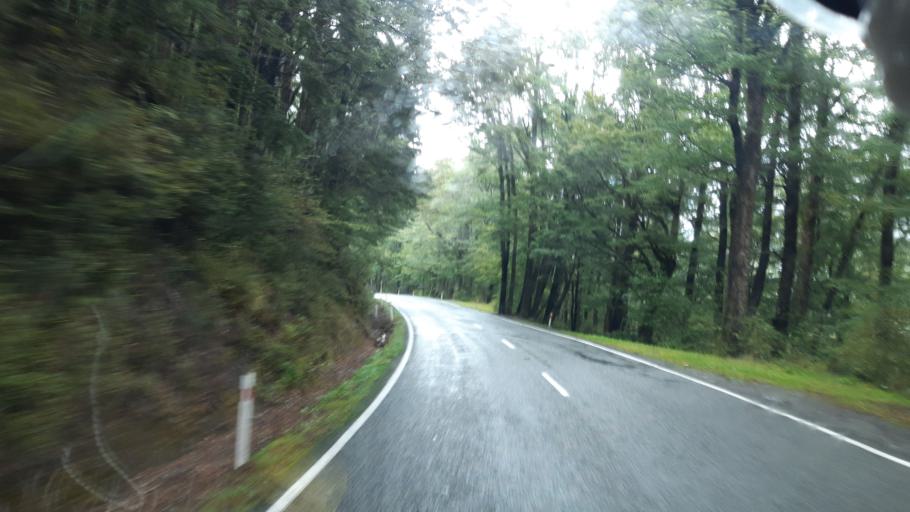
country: NZ
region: Canterbury
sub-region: Hurunui District
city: Amberley
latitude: -42.3767
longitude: 172.3575
